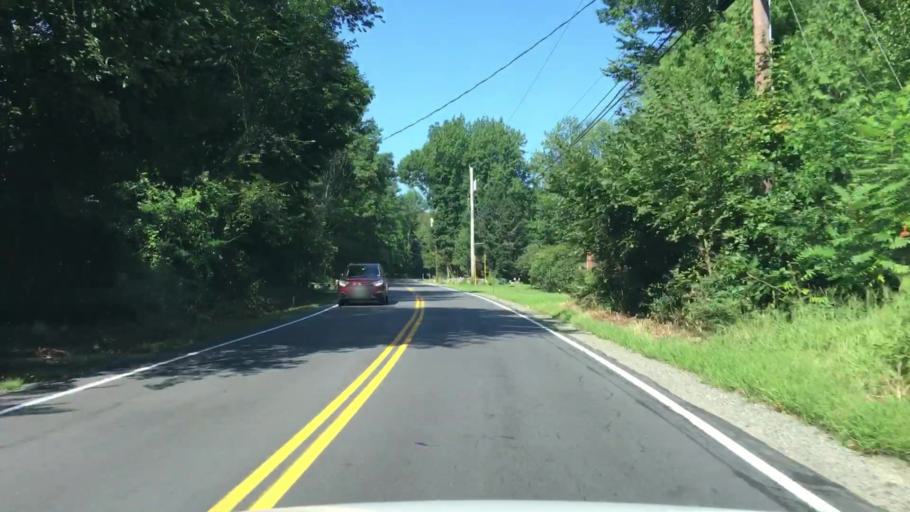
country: US
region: New Hampshire
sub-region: Rockingham County
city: Kensington
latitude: 42.9150
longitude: -70.9693
